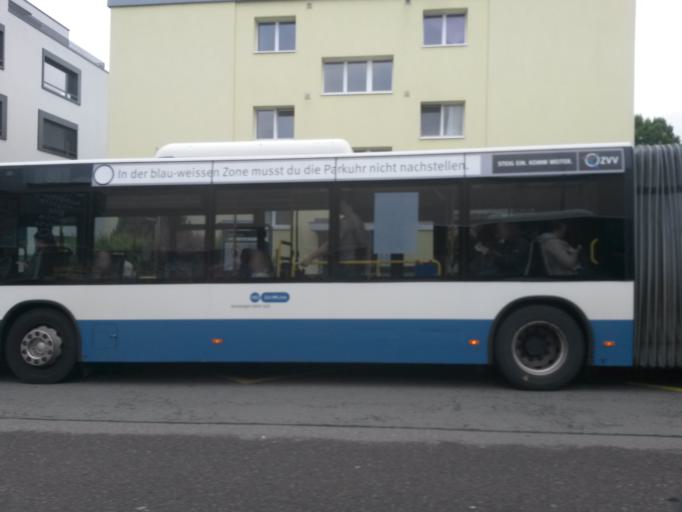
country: CH
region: Zurich
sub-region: Bezirk Zuerich
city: Zuerich (Kreis 11) / Oerlikon
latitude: 47.4133
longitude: 8.5310
